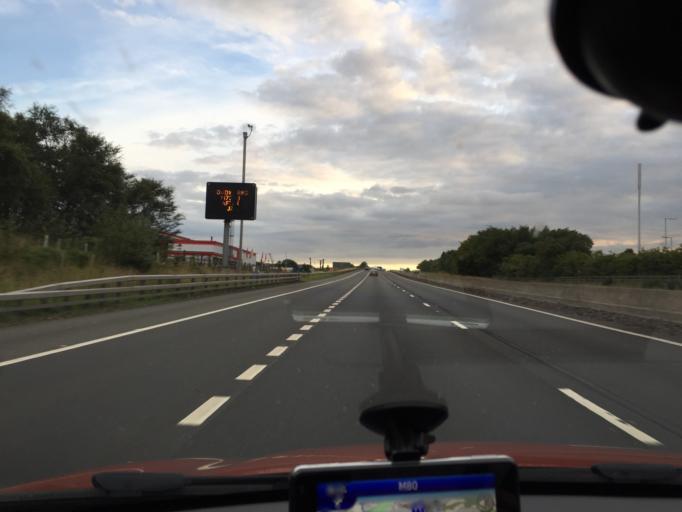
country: GB
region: Scotland
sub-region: North Lanarkshire
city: Cumbernauld
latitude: 55.9738
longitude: -3.9552
